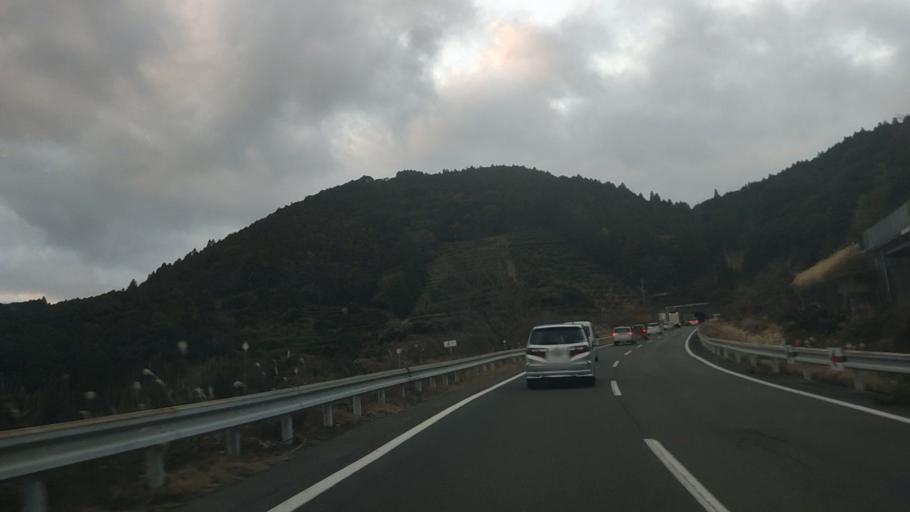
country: JP
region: Nagasaki
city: Obita
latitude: 32.8112
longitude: 129.9336
